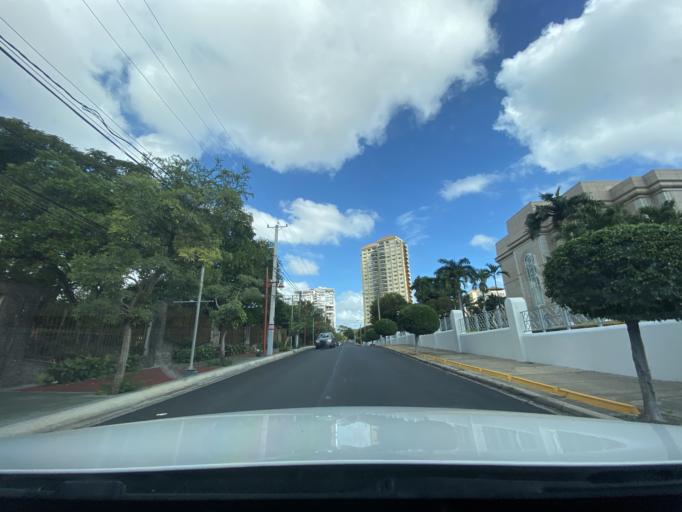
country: DO
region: Nacional
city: La Julia
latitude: 18.4663
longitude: -69.9175
